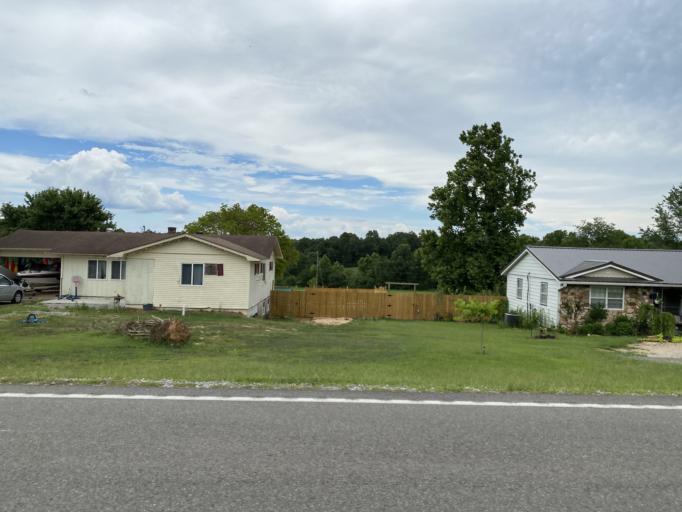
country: US
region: Arkansas
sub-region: Fulton County
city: Salem
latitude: 36.3625
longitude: -91.8307
